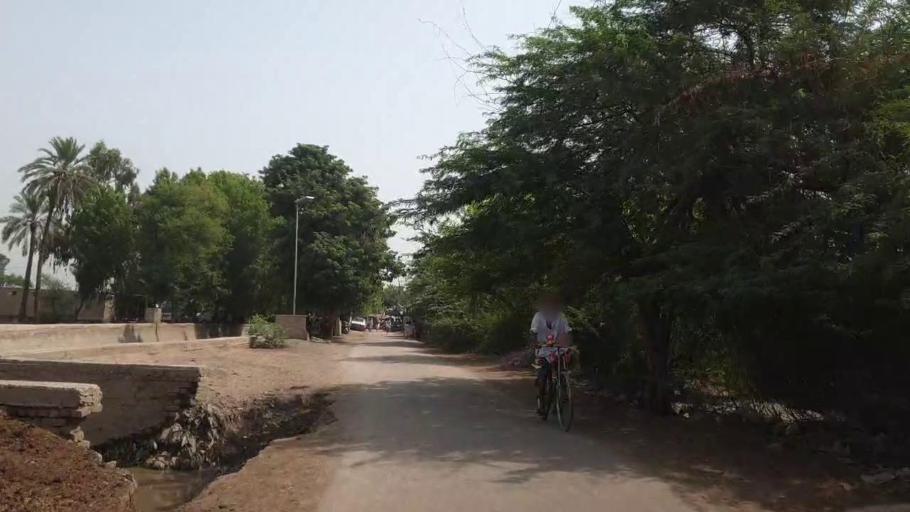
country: PK
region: Sindh
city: Gambat
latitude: 27.3829
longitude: 68.5158
